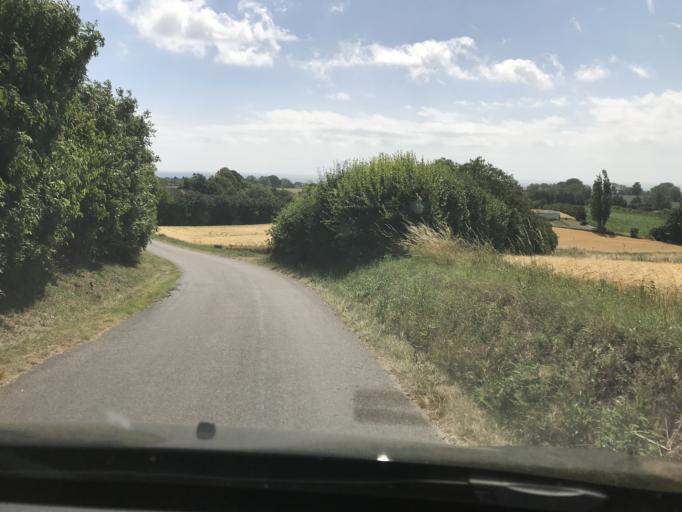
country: DK
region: South Denmark
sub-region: AEro Kommune
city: AEroskobing
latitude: 54.9001
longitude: 10.3066
